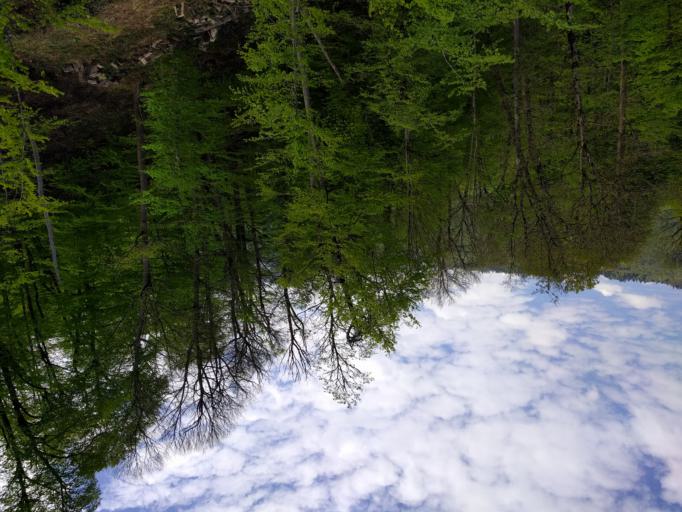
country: RU
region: Krasnodarskiy
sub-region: Sochi City
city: Krasnaya Polyana
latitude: 43.6656
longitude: 40.3080
